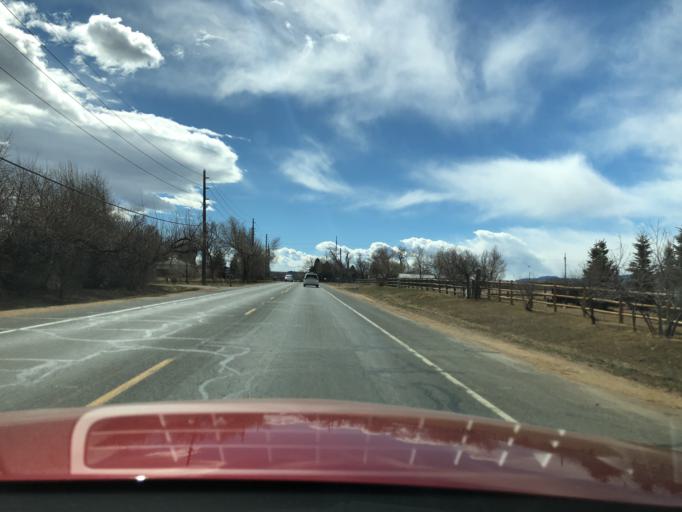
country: US
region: Colorado
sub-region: Boulder County
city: Gunbarrel
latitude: 40.0208
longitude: -105.1784
